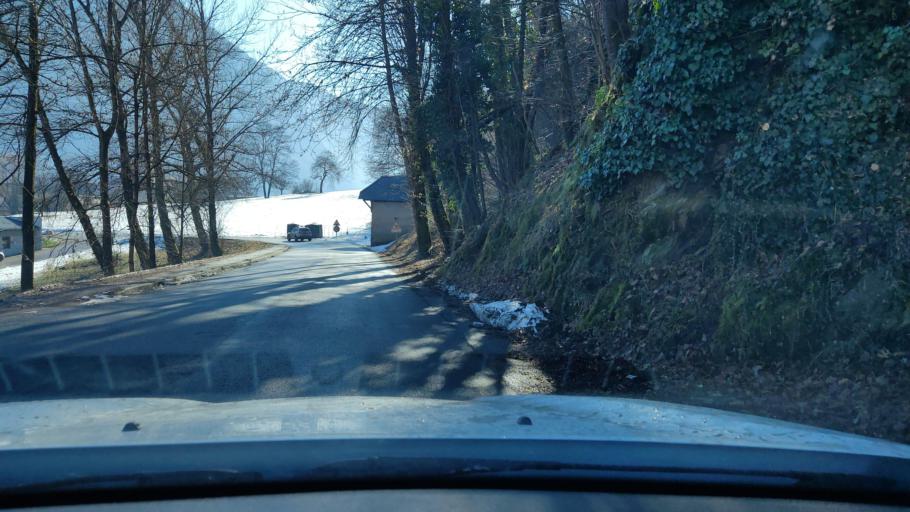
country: FR
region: Rhone-Alpes
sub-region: Departement de la Savoie
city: La Bathie
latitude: 45.5948
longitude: 6.4398
